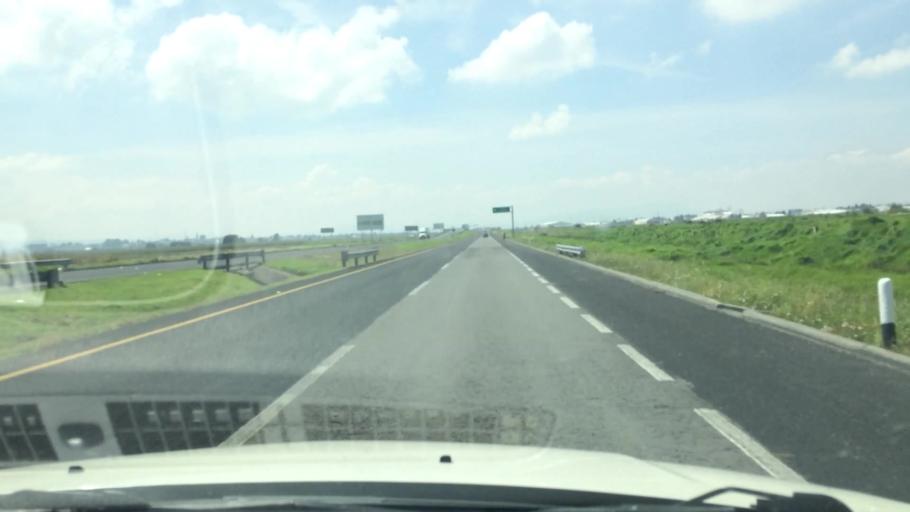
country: MX
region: Mexico
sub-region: Lerma
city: Colonia Isidro Fabela
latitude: 19.3148
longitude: -99.5221
